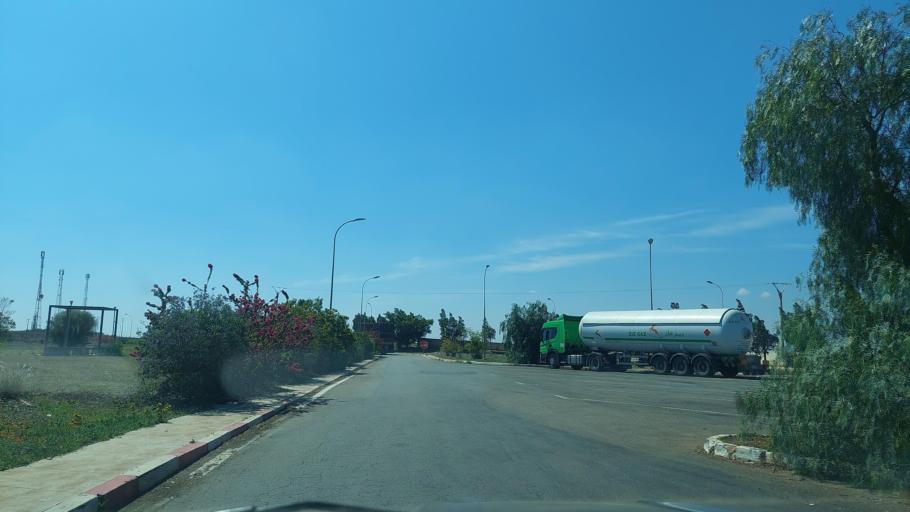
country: MA
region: Chaouia-Ouardigha
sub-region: Settat Province
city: Settat
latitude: 32.8963
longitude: -7.6700
